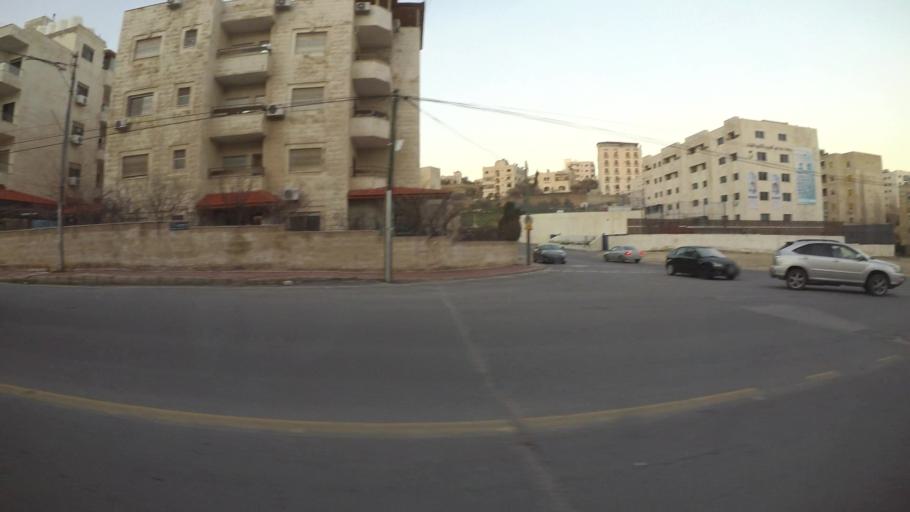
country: JO
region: Amman
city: Al Jubayhah
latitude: 32.0006
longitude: 35.8564
